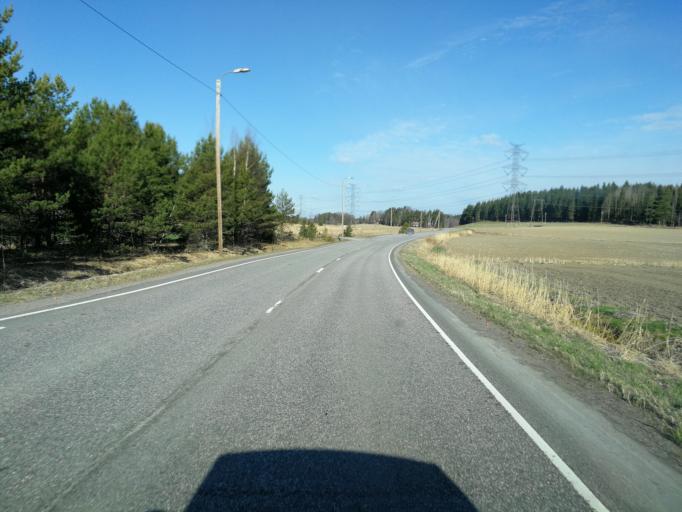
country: FI
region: Uusimaa
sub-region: Helsinki
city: Kirkkonummi
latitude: 60.2010
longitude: 24.5285
